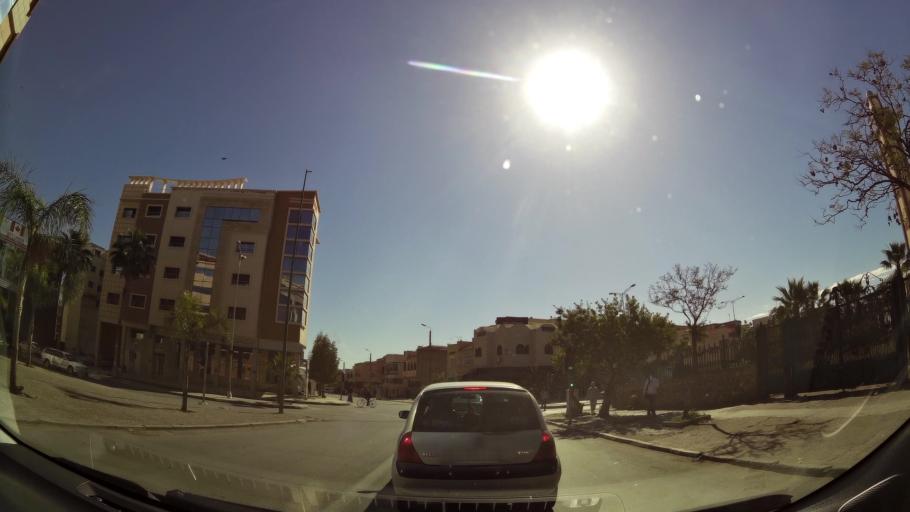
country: MA
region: Oriental
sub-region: Oujda-Angad
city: Oujda
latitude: 34.6564
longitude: -1.8985
